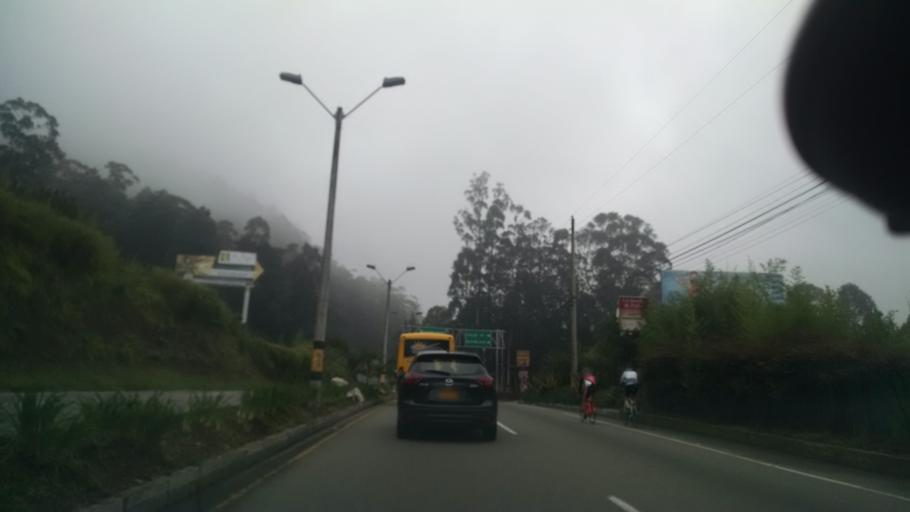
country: CO
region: Antioquia
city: Medellin
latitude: 6.2071
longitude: -75.5456
